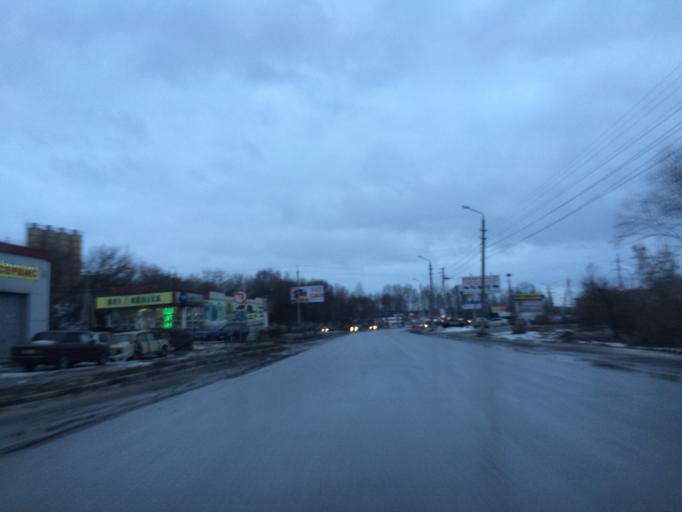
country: RU
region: Tula
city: Tula
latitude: 54.1697
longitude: 37.6341
